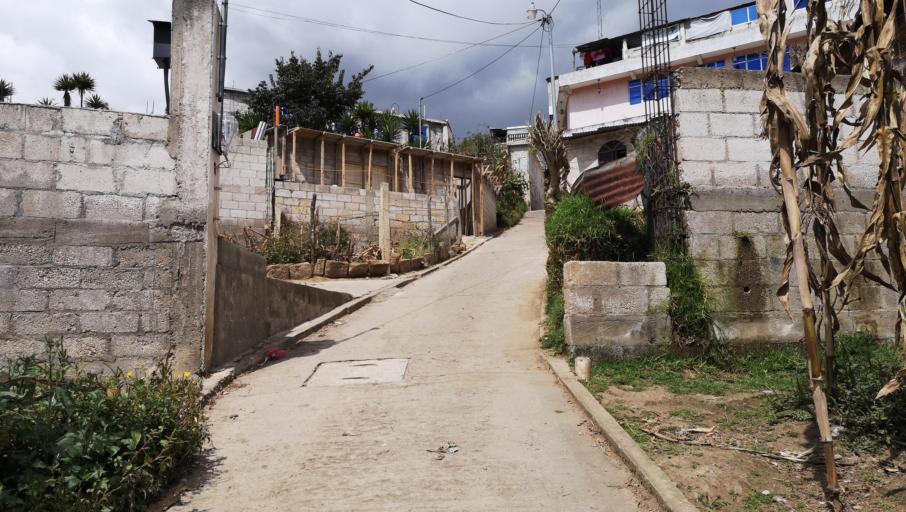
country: GT
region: Quetzaltenango
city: Cantel
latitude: 14.8186
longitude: -91.4475
